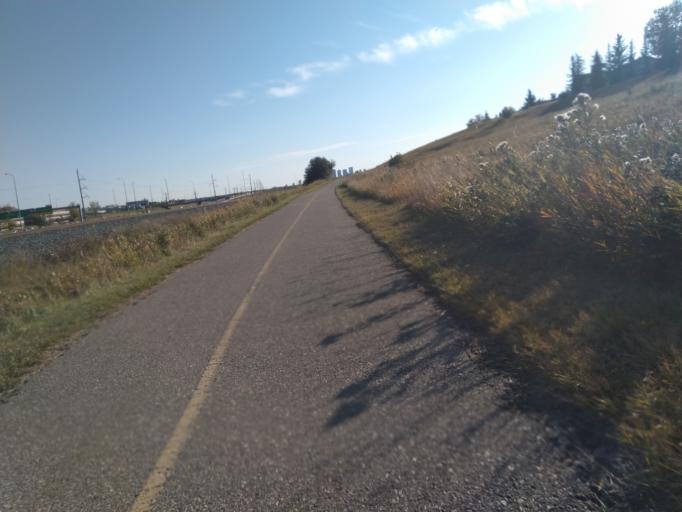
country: CA
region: Alberta
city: Calgary
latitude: 51.1173
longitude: -114.0485
